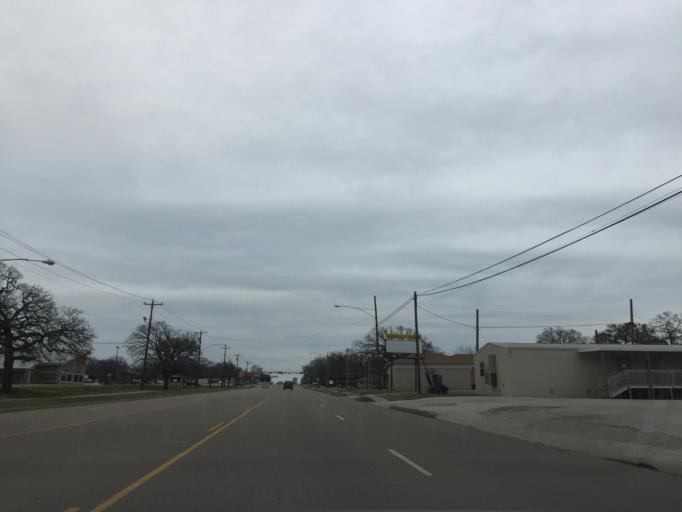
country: US
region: Texas
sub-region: Coryell County
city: Gatesville
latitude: 31.4347
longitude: -97.7243
